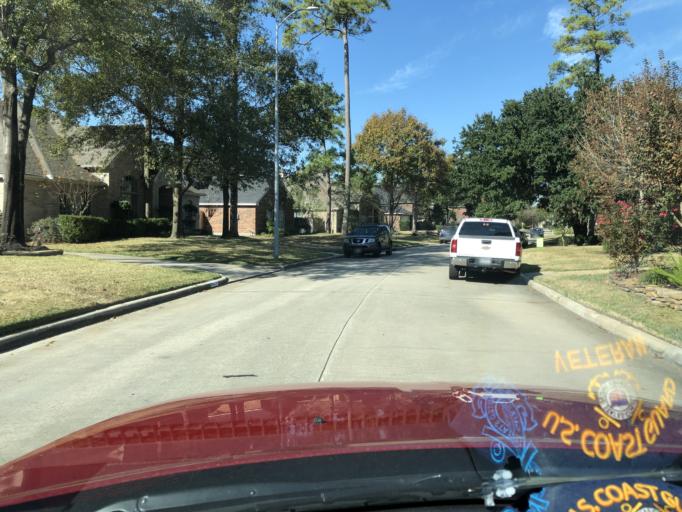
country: US
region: Texas
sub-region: Harris County
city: Tomball
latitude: 30.0205
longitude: -95.5544
